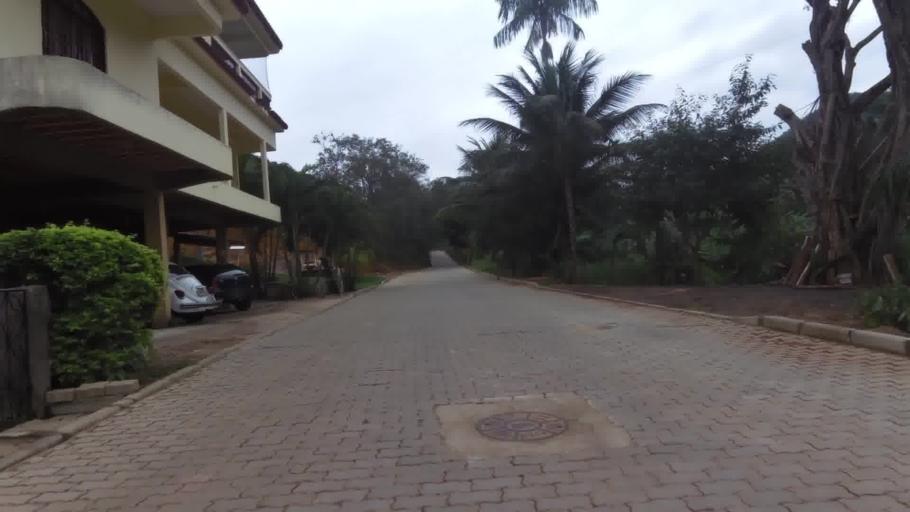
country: BR
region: Espirito Santo
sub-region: Iconha
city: Iconha
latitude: -20.7823
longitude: -40.8261
